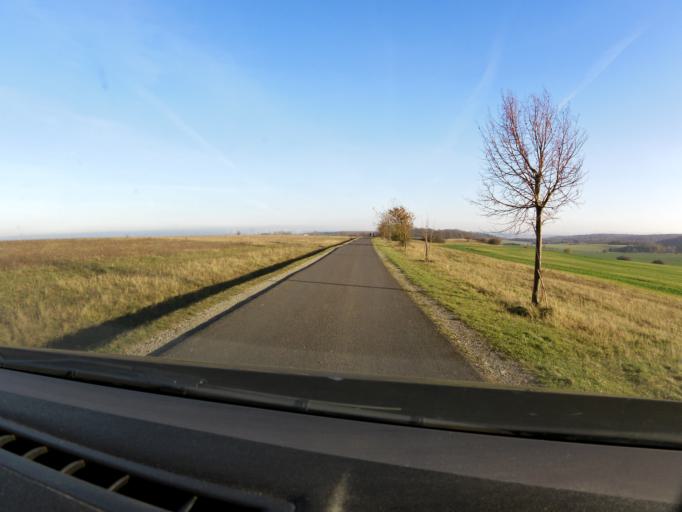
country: DE
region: Thuringia
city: Weberstedt
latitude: 51.0677
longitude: 10.4660
